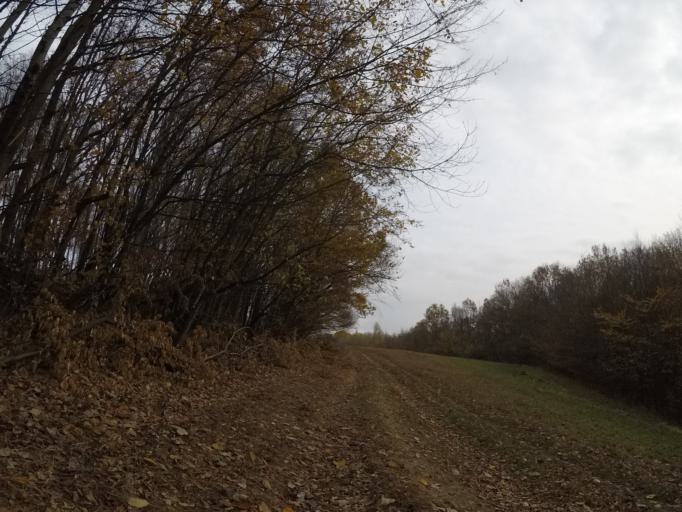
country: SK
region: Presovsky
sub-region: Okres Presov
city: Presov
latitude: 48.9413
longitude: 21.1431
